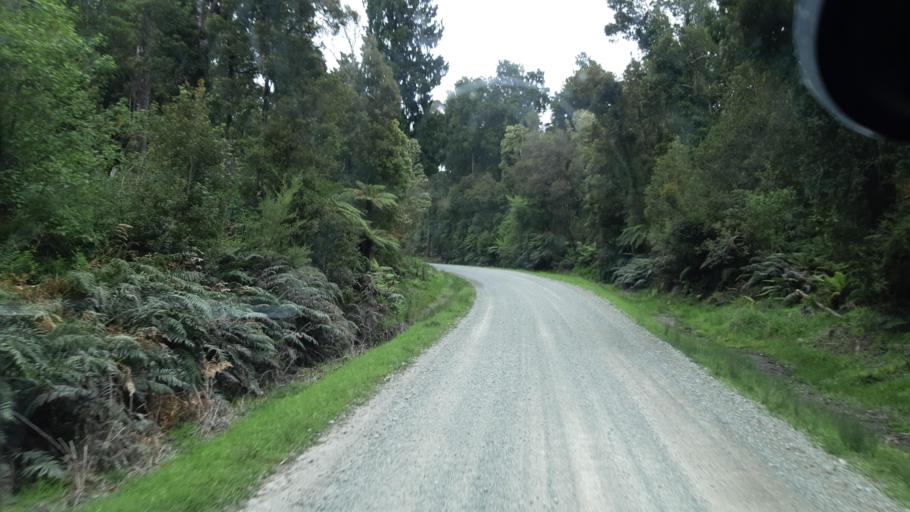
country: NZ
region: West Coast
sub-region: Grey District
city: Greymouth
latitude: -42.6475
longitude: 171.3196
